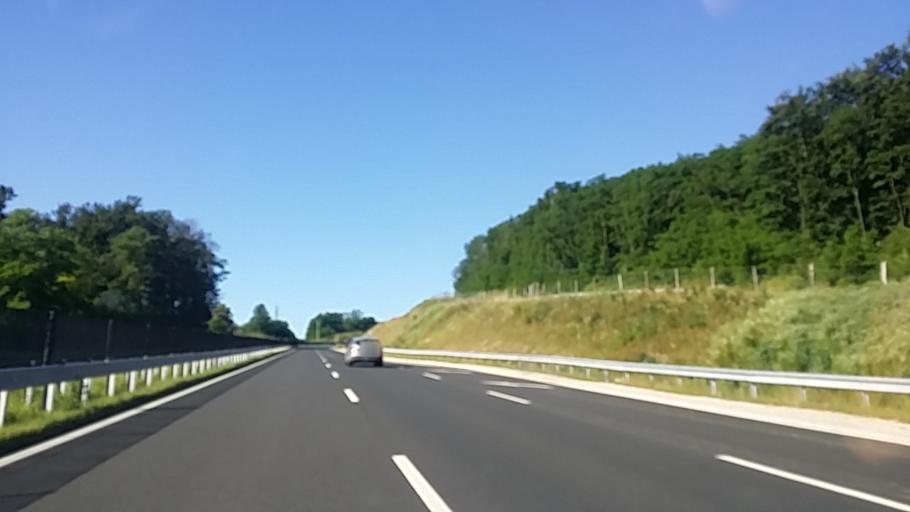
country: HU
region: Zala
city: Heviz
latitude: 46.7918
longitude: 17.1398
